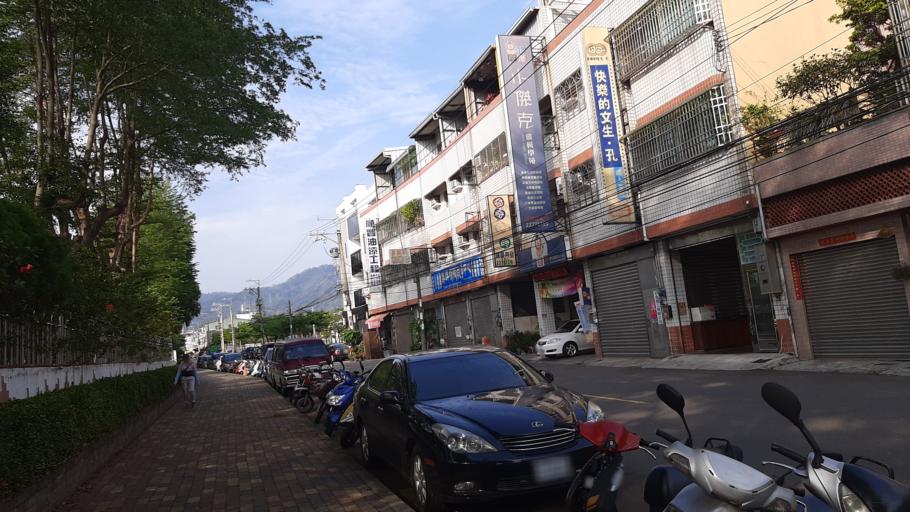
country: TW
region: Taiwan
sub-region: Taichung City
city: Taichung
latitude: 24.1232
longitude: 120.7238
